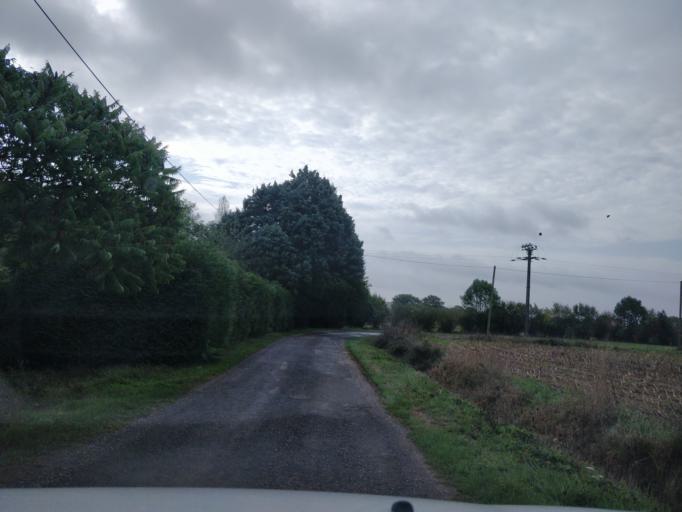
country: FR
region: Brittany
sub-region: Departement d'Ille-et-Vilaine
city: Liffre
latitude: 48.2152
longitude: -1.4783
